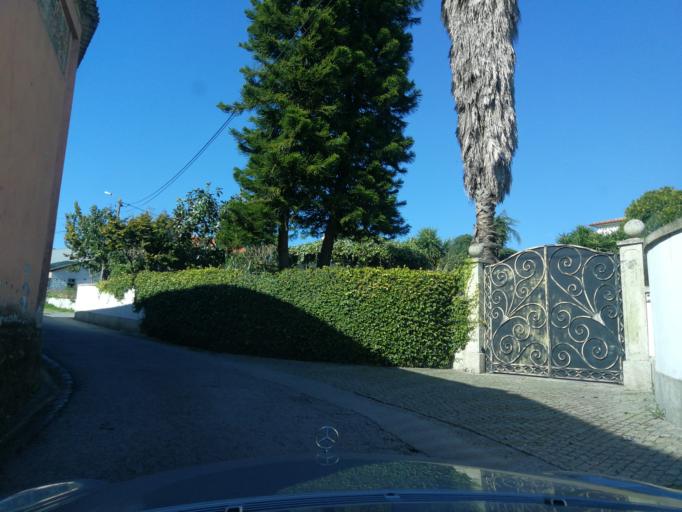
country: PT
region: Braga
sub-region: Vila Nova de Famalicao
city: Calendario
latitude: 41.3990
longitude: -8.5240
